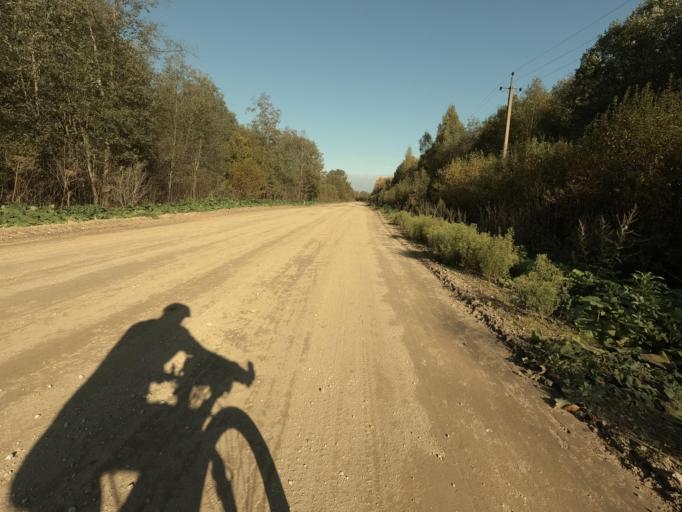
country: RU
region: Novgorod
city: Batetskiy
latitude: 58.8758
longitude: 30.7256
